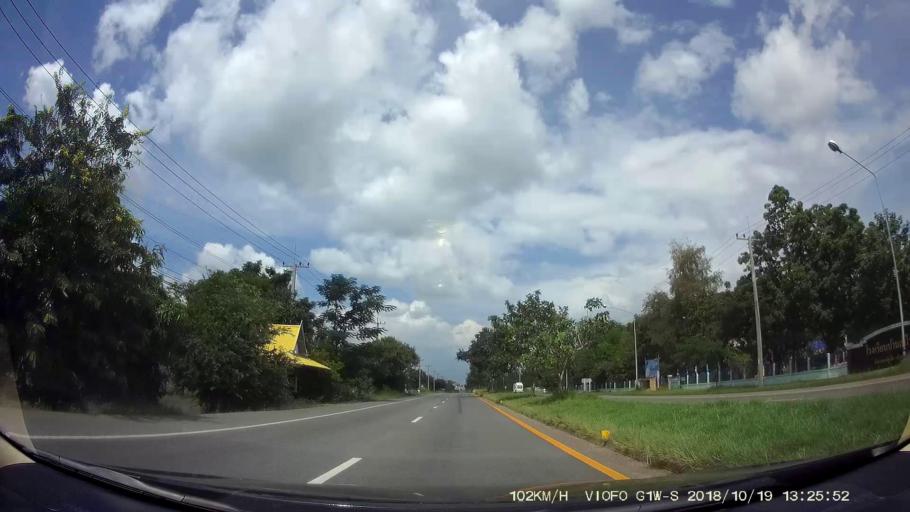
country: TH
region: Chaiyaphum
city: Chatturat
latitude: 15.5270
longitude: 101.8291
